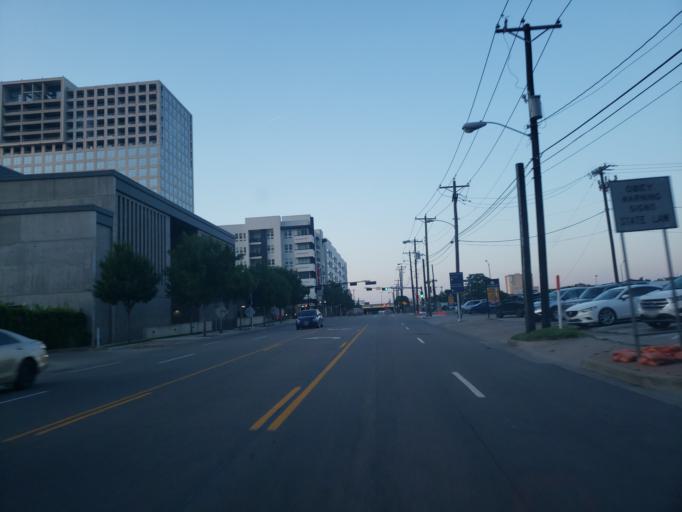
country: US
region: Texas
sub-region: Dallas County
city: Dallas
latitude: 32.7898
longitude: -96.7958
